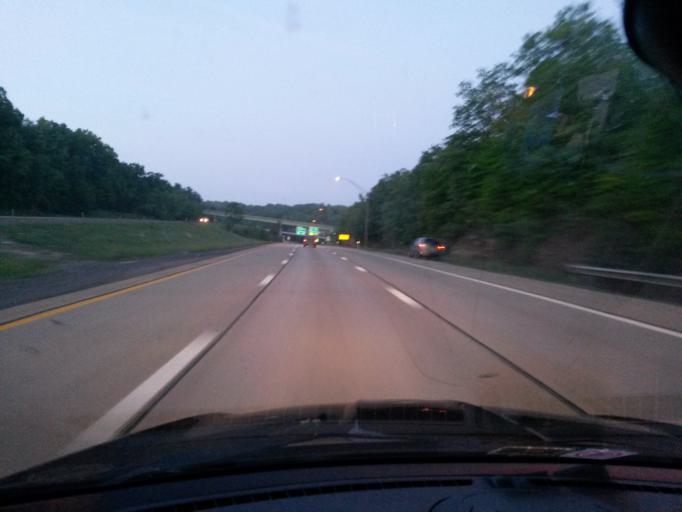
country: US
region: West Virginia
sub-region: Raleigh County
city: MacArthur
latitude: 37.7351
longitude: -81.1917
